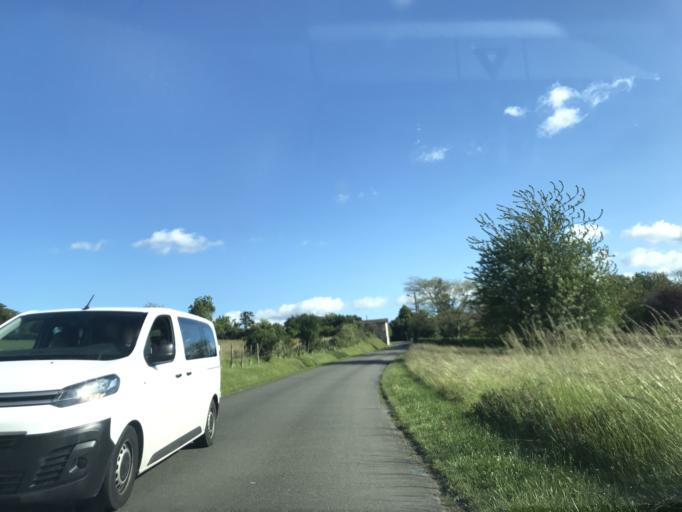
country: FR
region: Poitou-Charentes
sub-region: Departement de la Charente
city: Chalais
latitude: 45.2737
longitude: -0.0044
